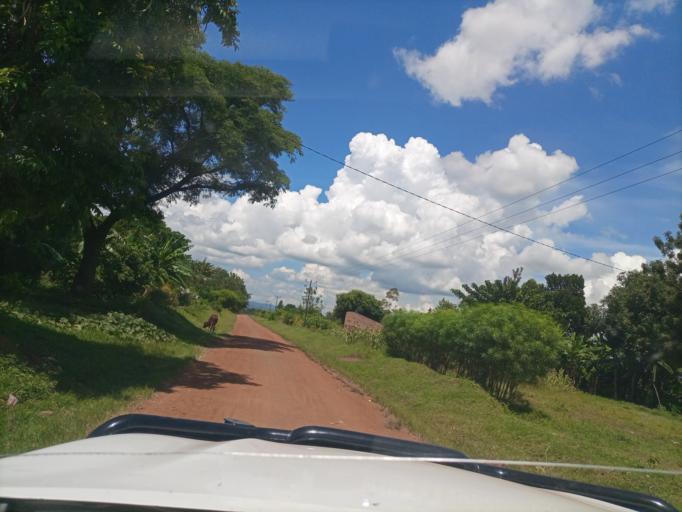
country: UG
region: Eastern Region
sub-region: Tororo District
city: Tororo
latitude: 0.6919
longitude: 34.0105
